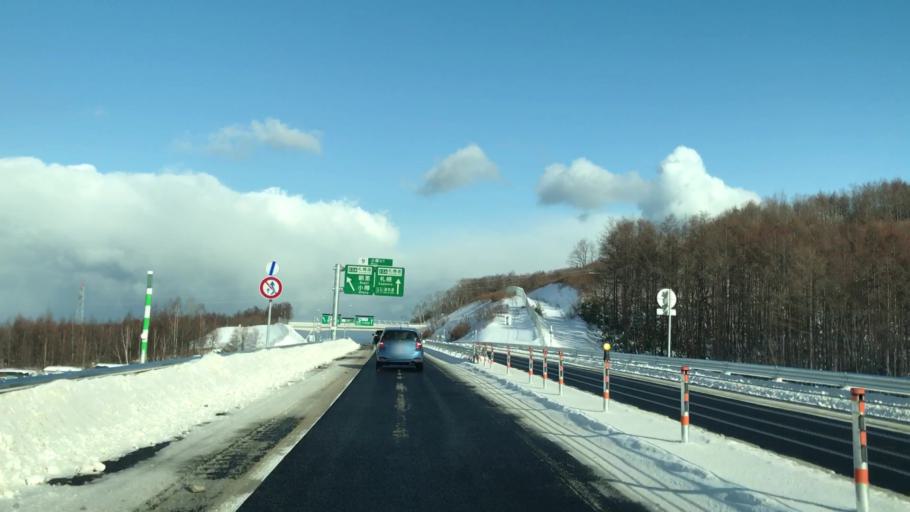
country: JP
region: Hokkaido
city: Otaru
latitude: 43.1612
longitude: 141.0556
